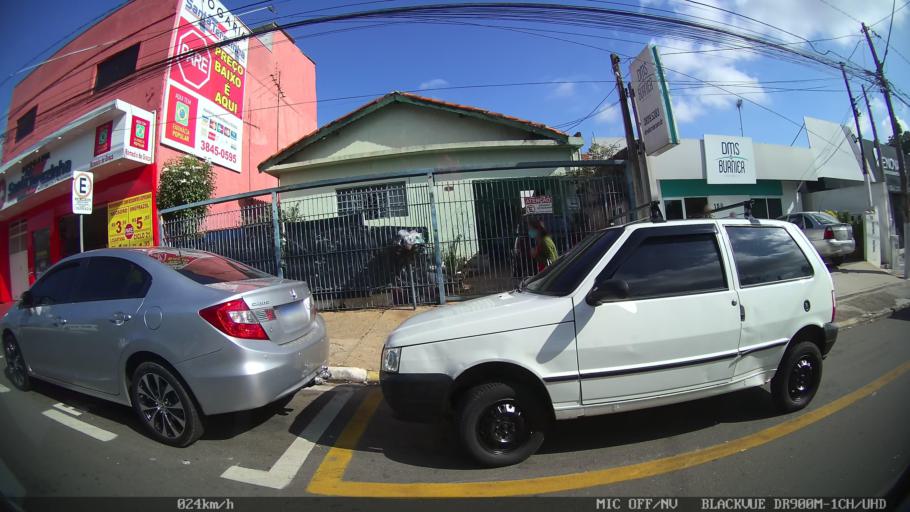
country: BR
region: Sao Paulo
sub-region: Hortolandia
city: Hortolandia
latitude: -22.8845
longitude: -47.1957
